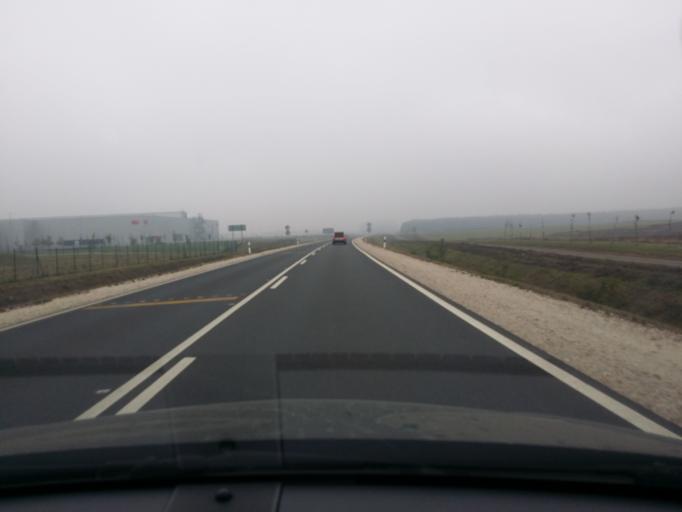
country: HU
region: Szabolcs-Szatmar-Bereg
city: Nyiregyhaza
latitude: 47.9454
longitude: 21.6518
